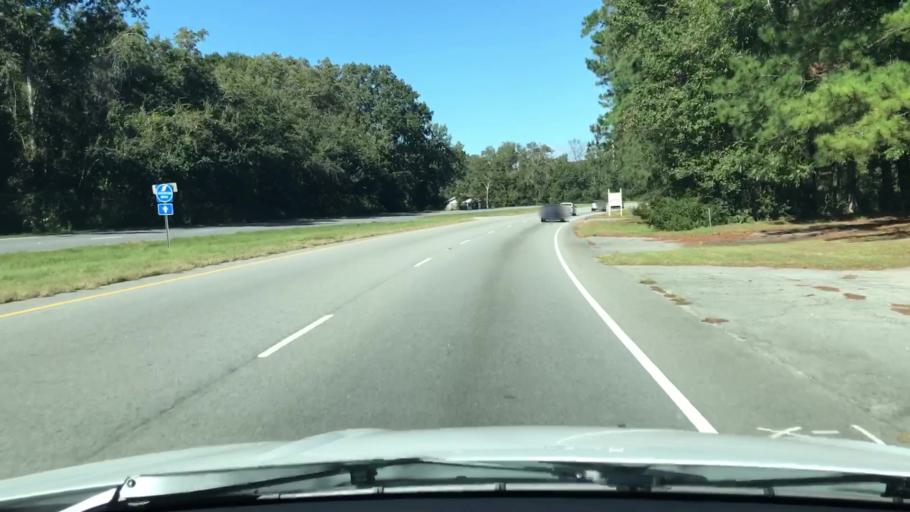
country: US
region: South Carolina
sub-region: Beaufort County
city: Laurel Bay
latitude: 32.5155
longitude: -80.7524
